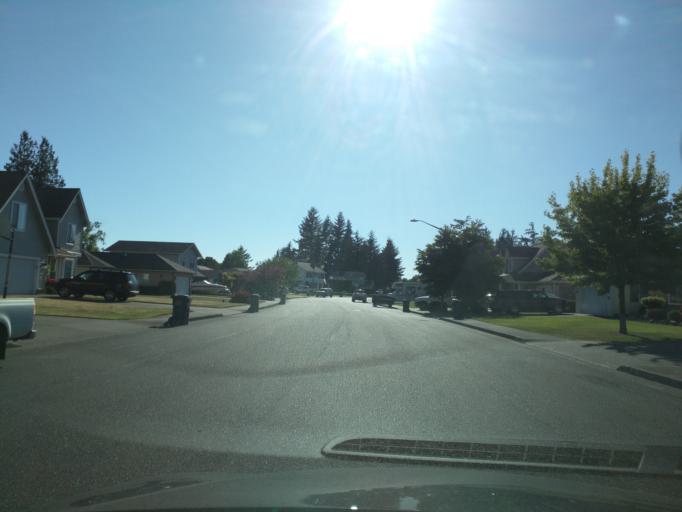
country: US
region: Washington
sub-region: Whatcom County
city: Lynden
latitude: 48.9568
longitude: -122.4487
